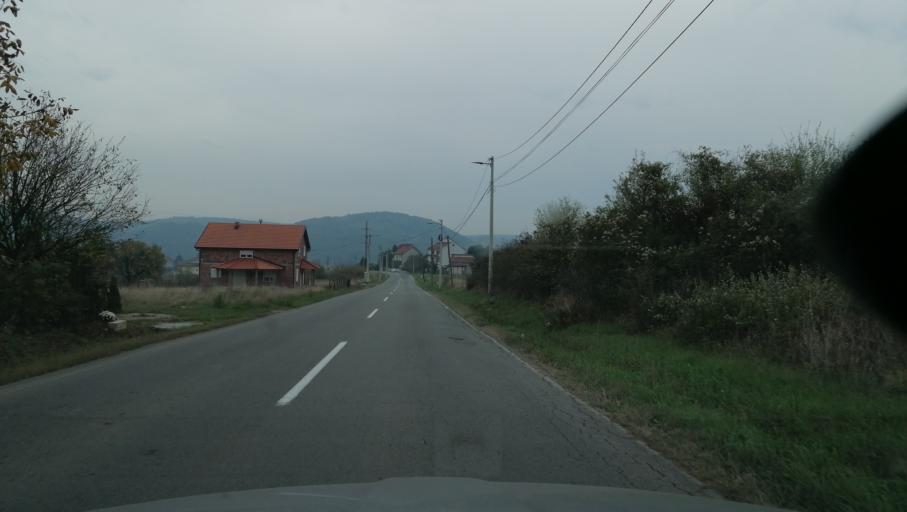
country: RS
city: Rusanj
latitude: 44.6759
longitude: 20.5053
